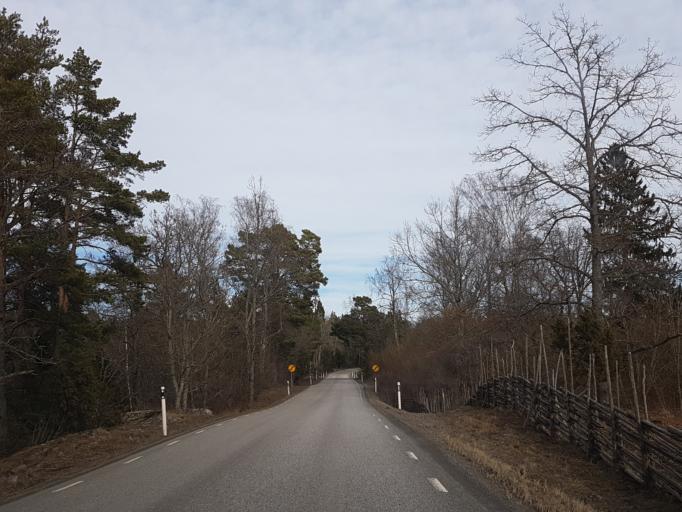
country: SE
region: Stockholm
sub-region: Norrtalje Kommun
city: Bjorko
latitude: 59.6670
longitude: 18.8684
